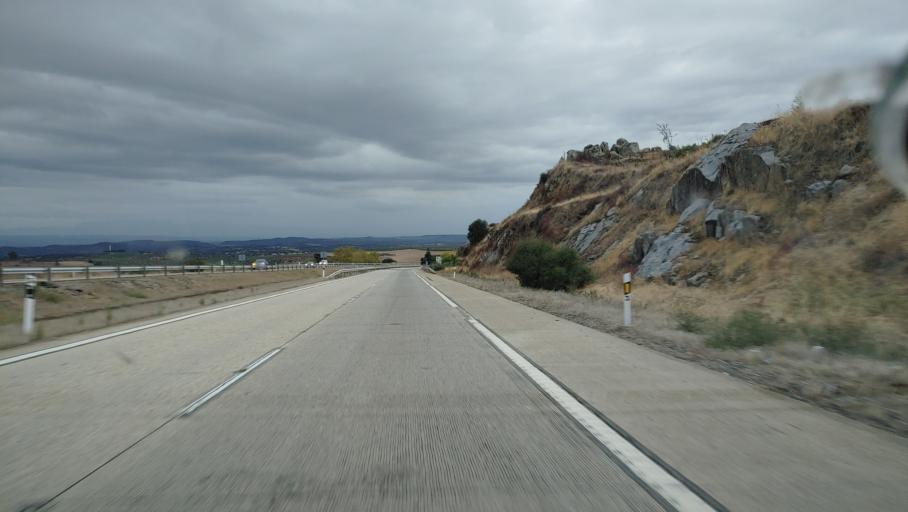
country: ES
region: Andalusia
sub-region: Provincia de Jaen
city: La Carolina
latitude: 38.3046
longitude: -3.5785
